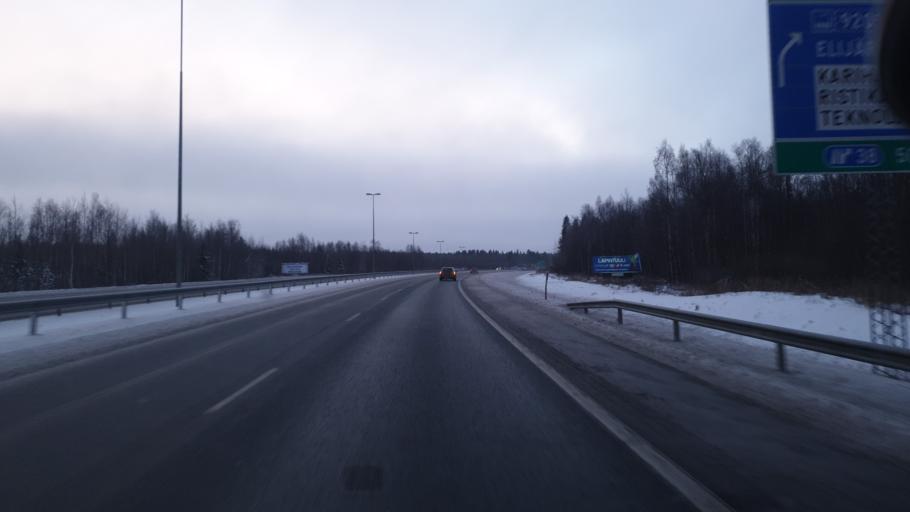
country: FI
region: Lapland
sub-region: Kemi-Tornio
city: Kemi
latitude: 65.7683
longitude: 24.5717
